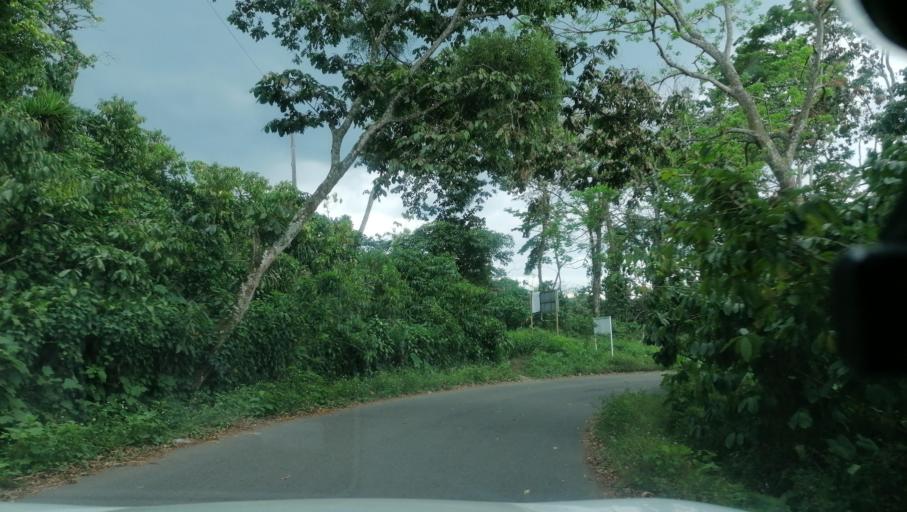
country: MX
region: Chiapas
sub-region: Cacahoatan
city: Benito Juarez
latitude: 15.0713
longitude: -92.1910
